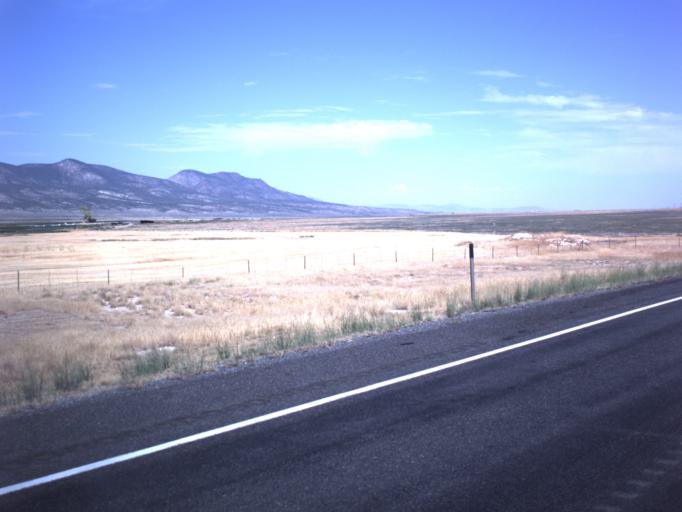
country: US
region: Utah
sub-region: Sanpete County
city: Gunnison
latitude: 39.2344
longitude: -111.8479
